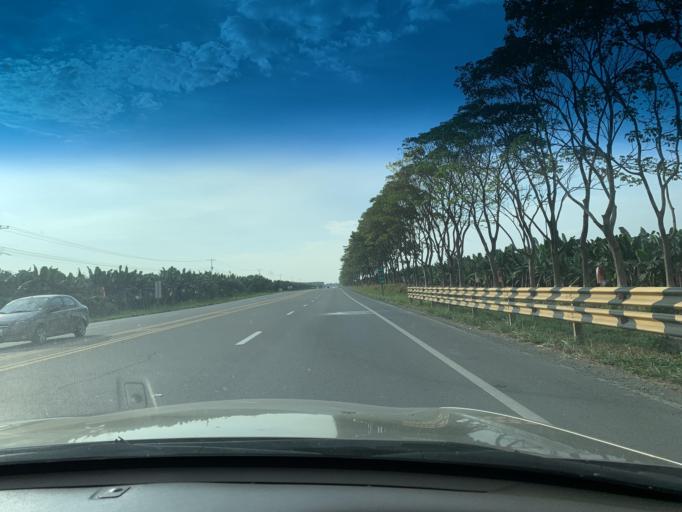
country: EC
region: Guayas
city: Coronel Marcelino Mariduena
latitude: -2.2727
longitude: -79.5377
